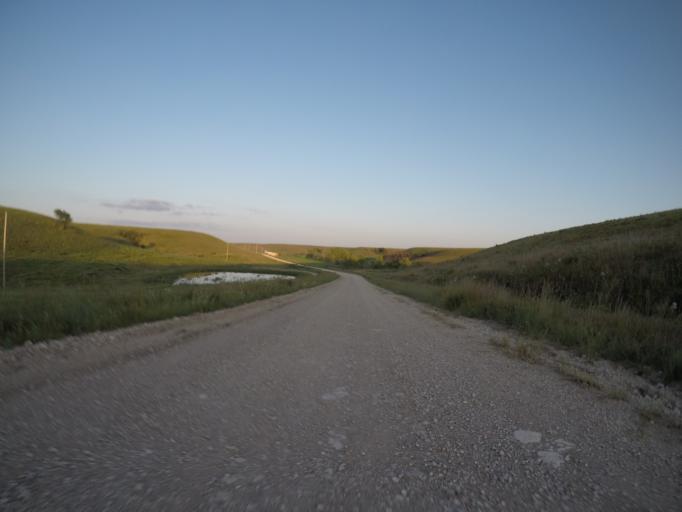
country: US
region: Kansas
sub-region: Riley County
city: Ogden
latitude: 39.0061
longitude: -96.6245
